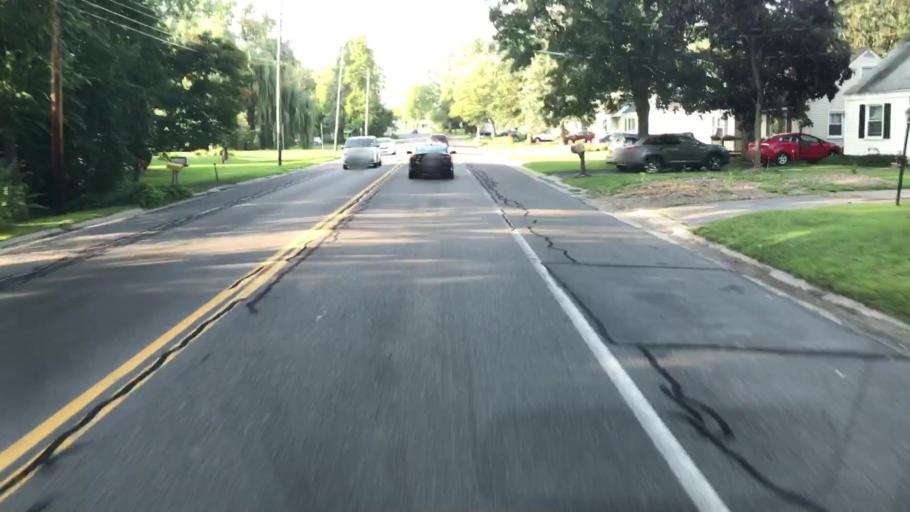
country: US
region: New York
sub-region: Onondaga County
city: Mattydale
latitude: 43.1153
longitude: -76.1594
